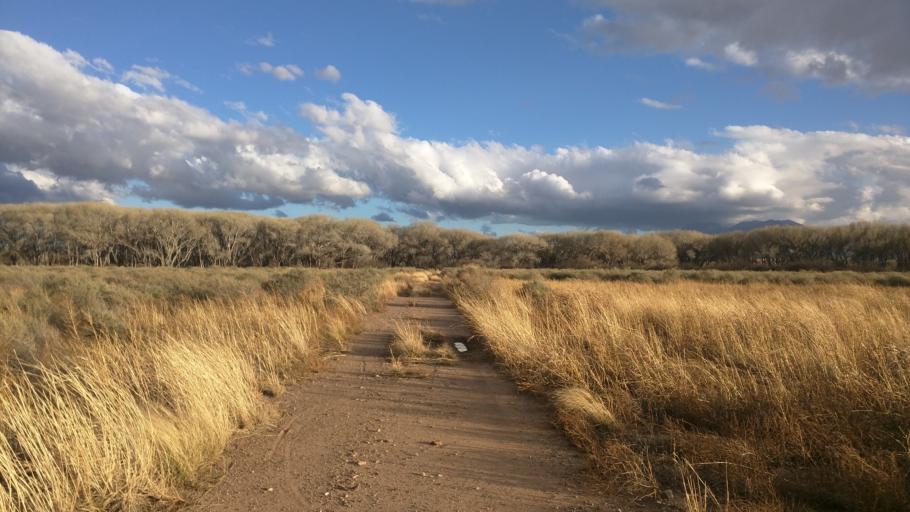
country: US
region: Arizona
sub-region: Cochise County
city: Sierra Vista Southeast
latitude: 31.3690
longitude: -110.1220
